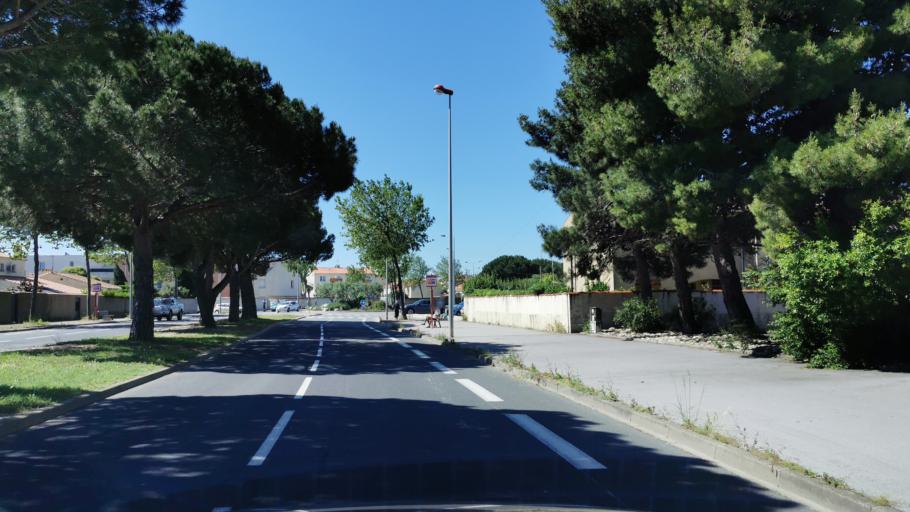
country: FR
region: Languedoc-Roussillon
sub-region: Departement de l'Aude
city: Narbonne
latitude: 43.1867
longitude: 2.9829
